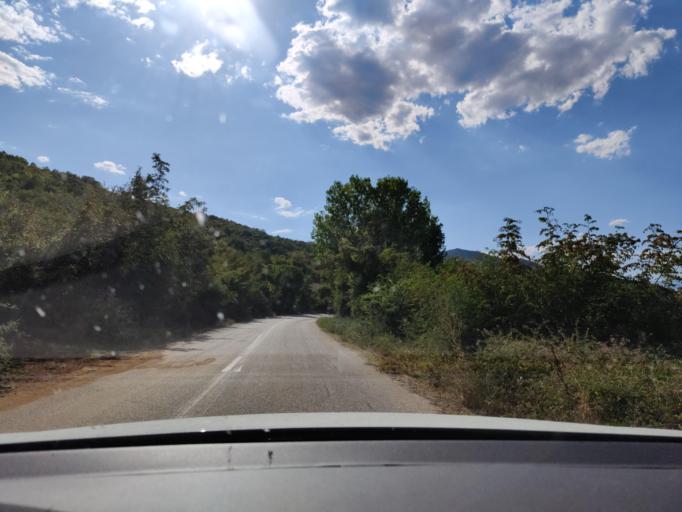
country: GR
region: Central Macedonia
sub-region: Nomos Serron
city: Chrysochorafa
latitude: 41.1591
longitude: 23.1916
